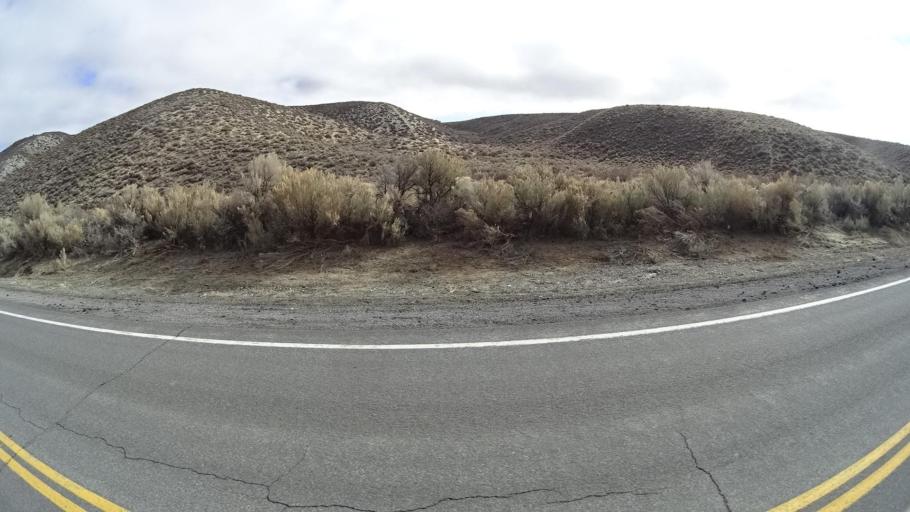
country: US
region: Nevada
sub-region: Washoe County
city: Cold Springs
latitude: 39.8070
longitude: -119.9320
